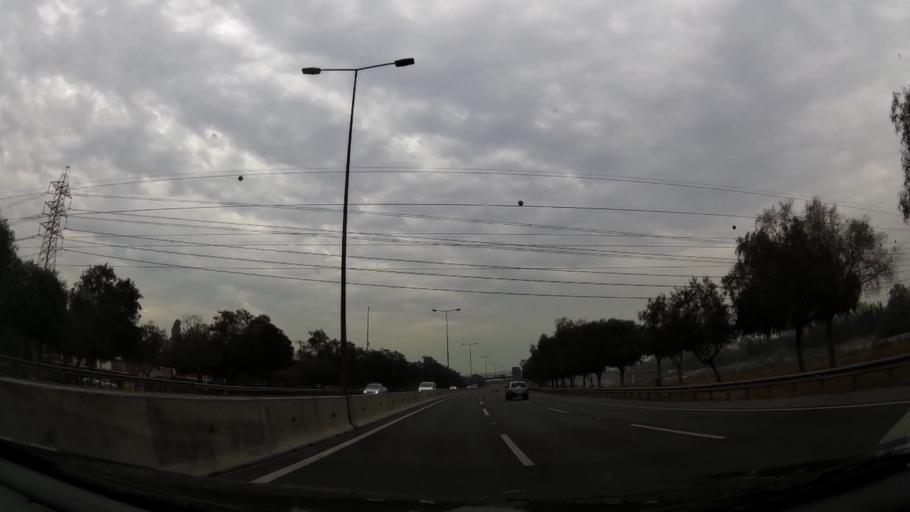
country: CL
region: Santiago Metropolitan
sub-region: Provincia de Santiago
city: Lo Prado
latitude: -33.4116
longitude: -70.7329
